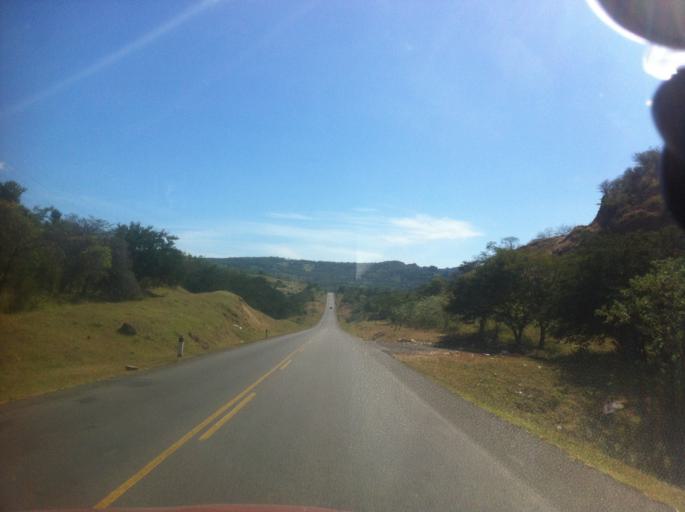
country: NI
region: Boaco
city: Teustepe
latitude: 12.3744
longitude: -85.8772
